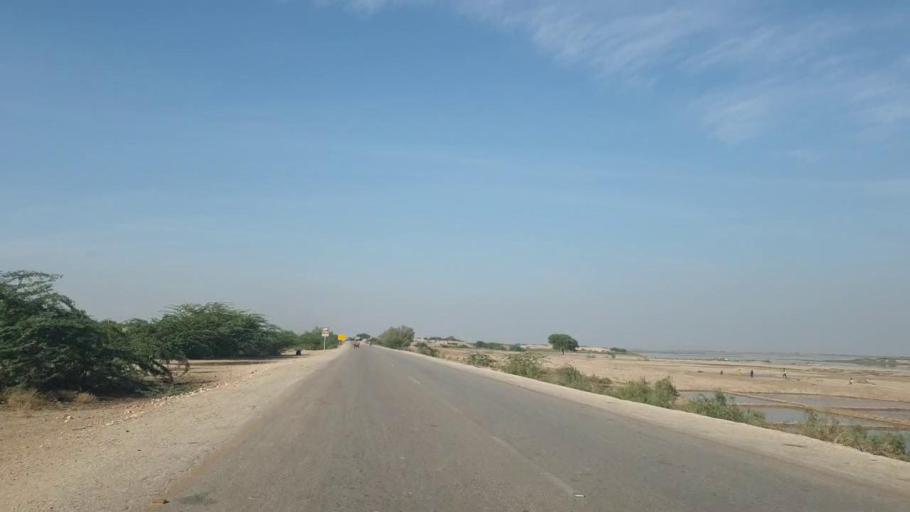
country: PK
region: Sindh
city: Sehwan
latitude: 26.3807
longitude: 67.8720
